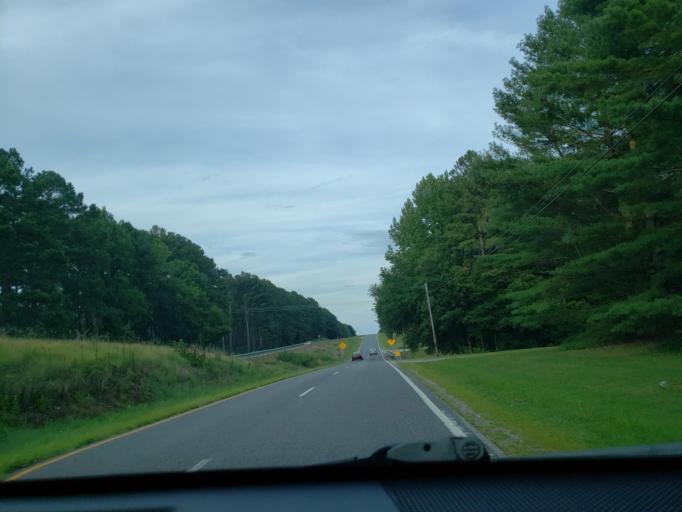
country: US
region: Virginia
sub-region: Brunswick County
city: Lawrenceville
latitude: 36.7451
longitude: -77.8739
